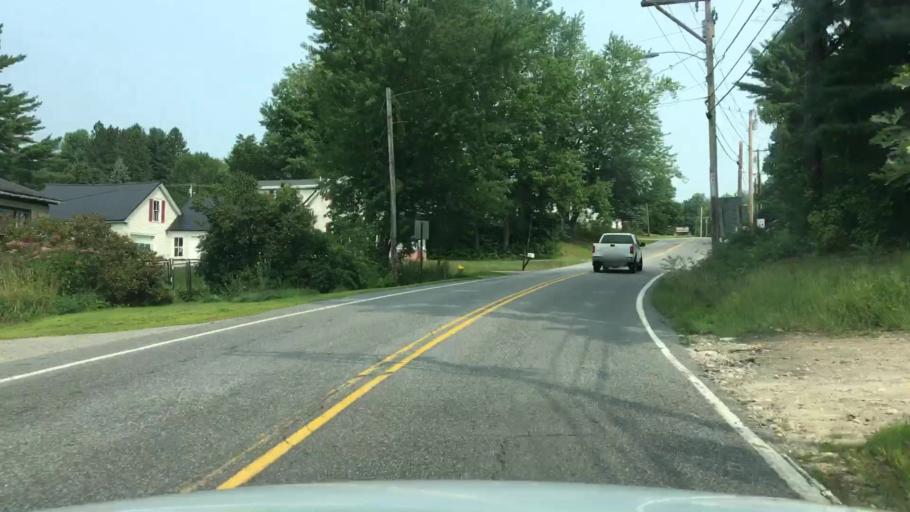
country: US
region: Maine
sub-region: Androscoggin County
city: Livermore Falls
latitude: 44.4798
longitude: -70.1872
